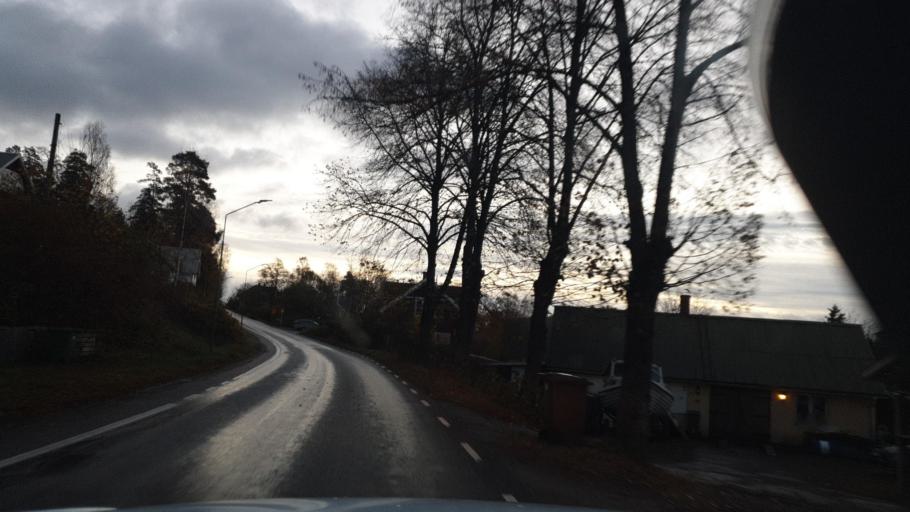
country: SE
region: Vaermland
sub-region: Arvika Kommun
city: Arvika
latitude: 59.6252
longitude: 12.8366
